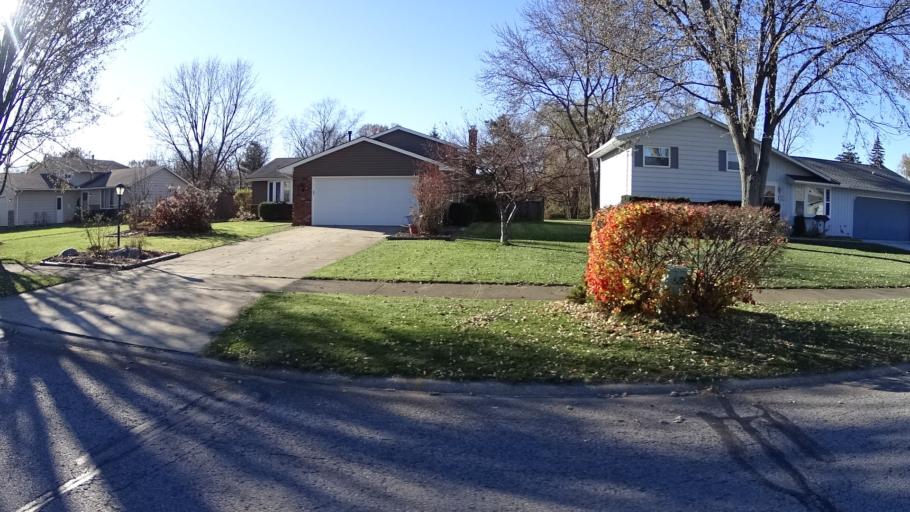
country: US
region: Ohio
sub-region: Lorain County
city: North Ridgeville
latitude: 41.4020
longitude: -82.0165
